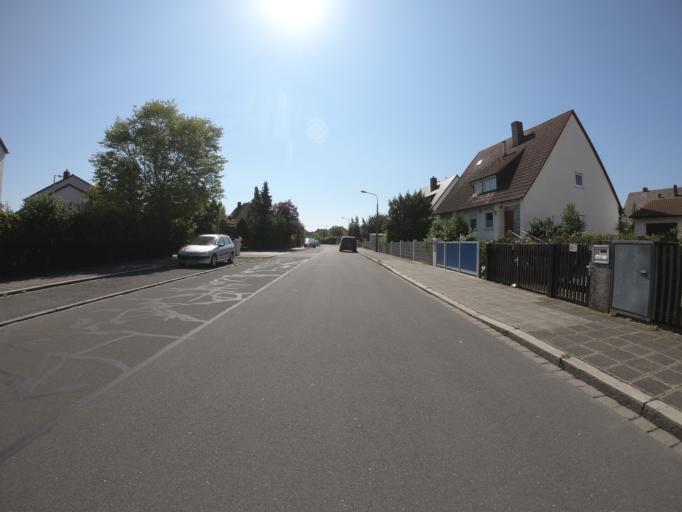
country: DE
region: Bavaria
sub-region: Regierungsbezirk Mittelfranken
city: Stein
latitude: 49.4106
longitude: 11.0277
